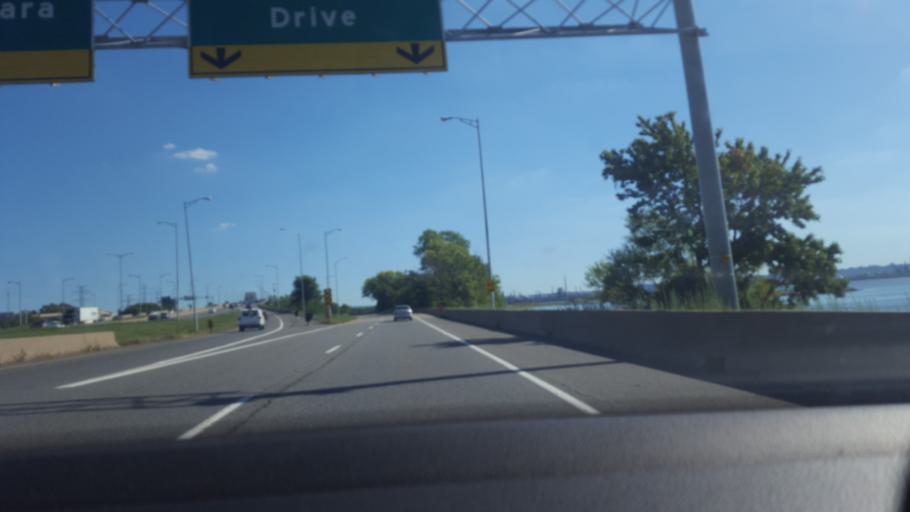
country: CA
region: Ontario
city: Hamilton
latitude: 43.3106
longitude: -79.8045
